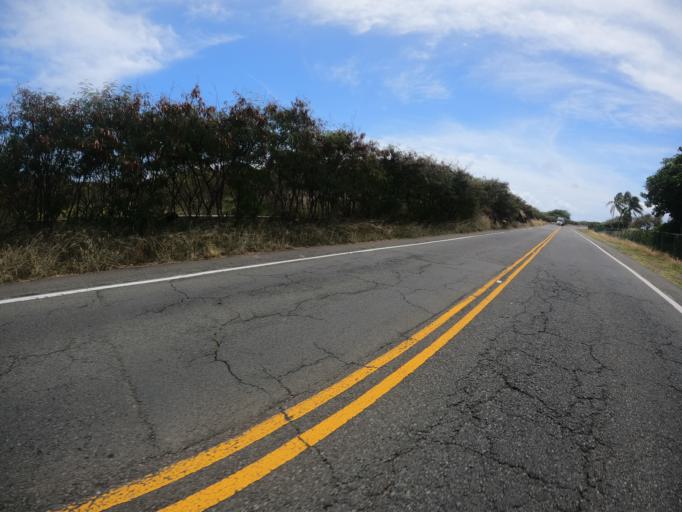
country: US
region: Hawaii
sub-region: Honolulu County
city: Waimanalo Beach
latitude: 21.2956
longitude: -157.6623
